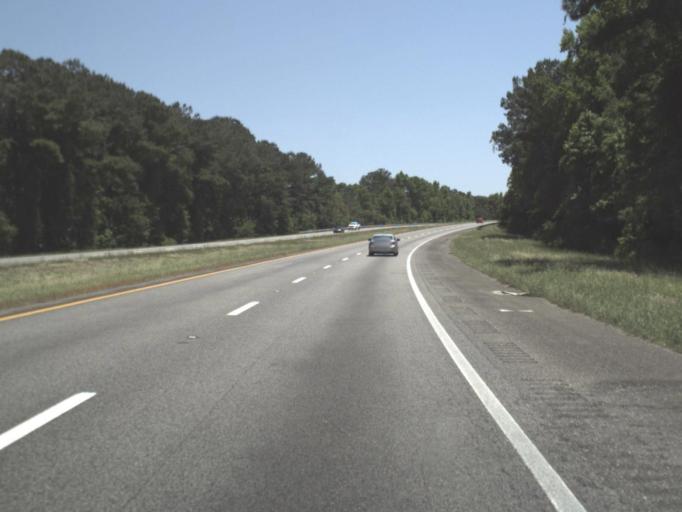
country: US
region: Florida
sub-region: Jefferson County
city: Monticello
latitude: 30.4863
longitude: -83.9525
